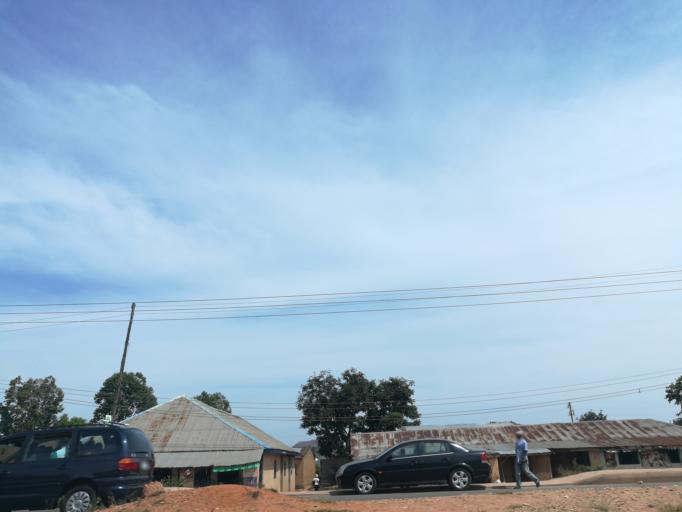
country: NG
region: Plateau
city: Bukuru
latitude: 9.7655
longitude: 8.8599
